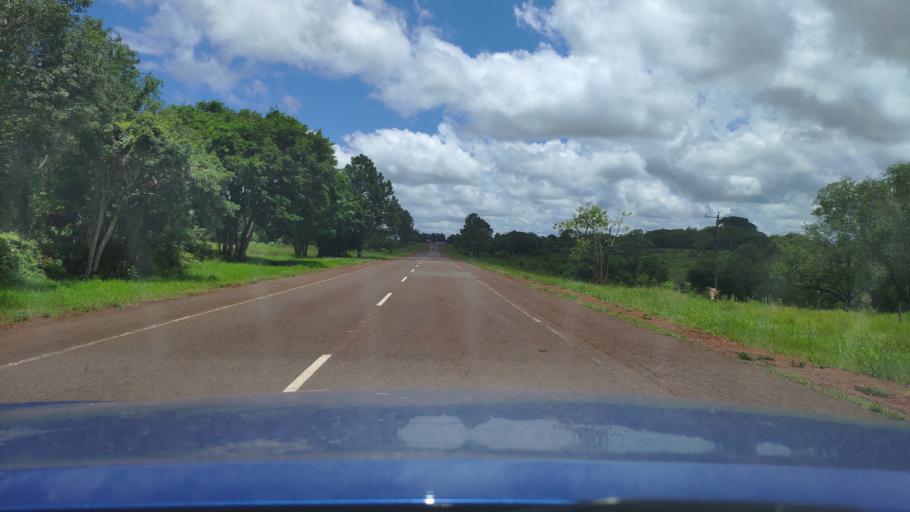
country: AR
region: Misiones
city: Dos Arroyos
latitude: -27.7467
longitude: -55.2595
